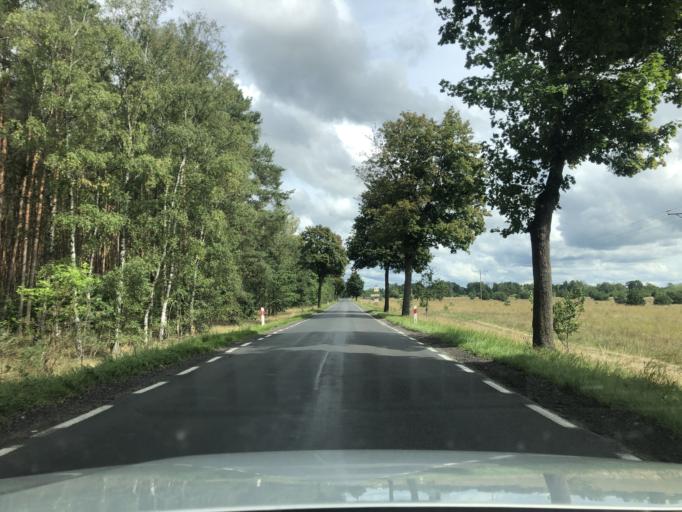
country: PL
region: Greater Poland Voivodeship
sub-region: Powiat czarnkowsko-trzcianecki
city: Krzyz Wielkopolski
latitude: 52.8675
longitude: 15.9729
